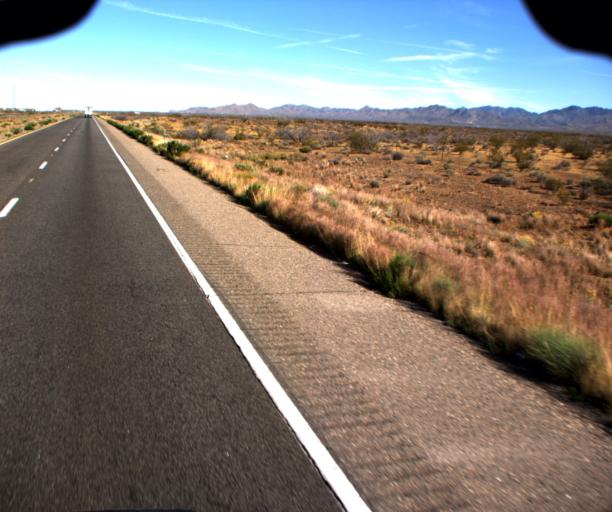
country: US
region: Arizona
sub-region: Mohave County
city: Golden Valley
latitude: 35.3238
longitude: -114.2063
